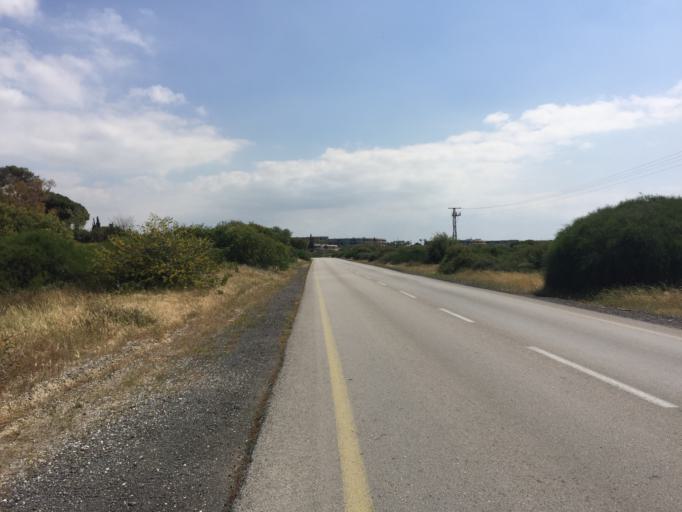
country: IL
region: Haifa
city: Qesarya
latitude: 32.4932
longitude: 34.8985
